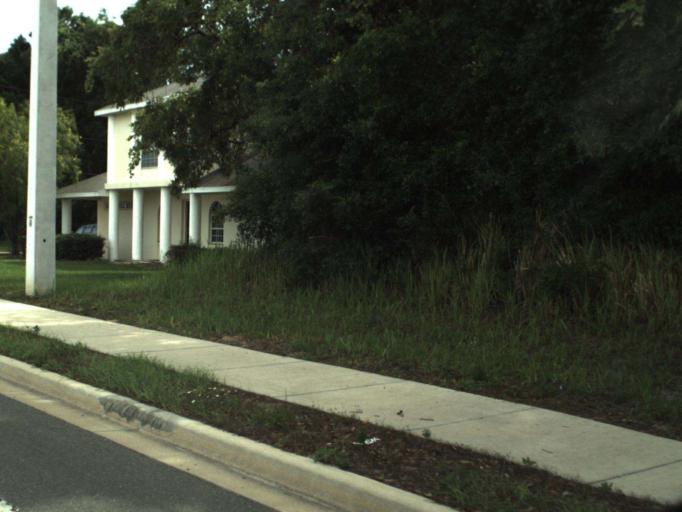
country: US
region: Florida
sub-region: Marion County
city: Silver Springs Shores
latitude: 29.1670
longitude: -82.0538
